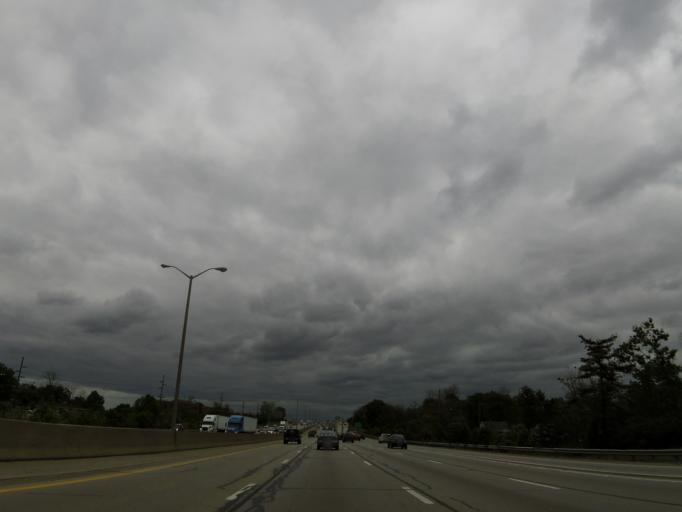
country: US
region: Kentucky
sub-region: Boone County
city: Florence
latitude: 39.0050
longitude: -84.6433
